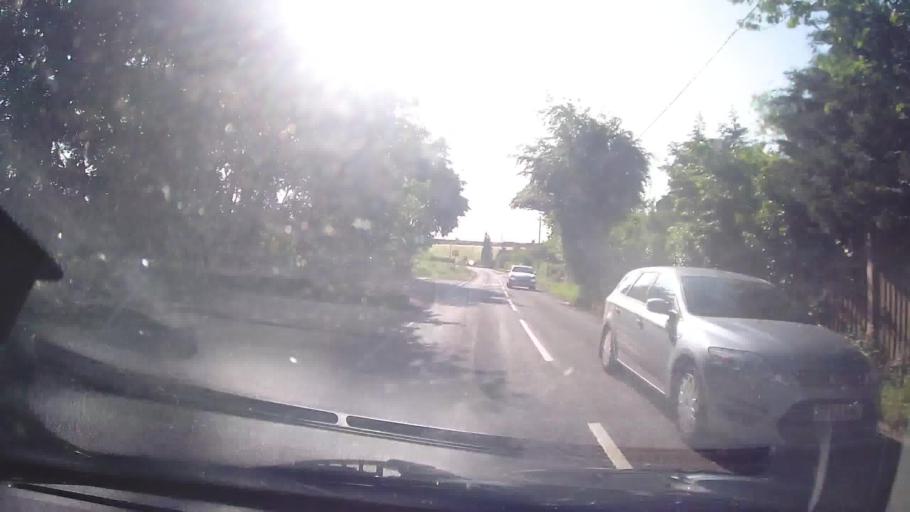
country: GB
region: England
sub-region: Shropshire
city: Withington
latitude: 52.7350
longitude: -2.5654
